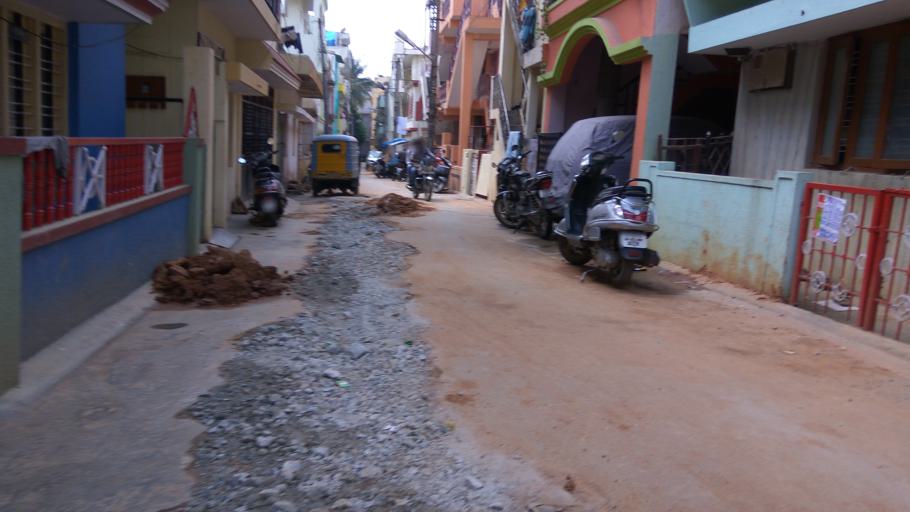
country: IN
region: Karnataka
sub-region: Bangalore Urban
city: Bangalore
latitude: 12.9741
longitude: 77.6390
